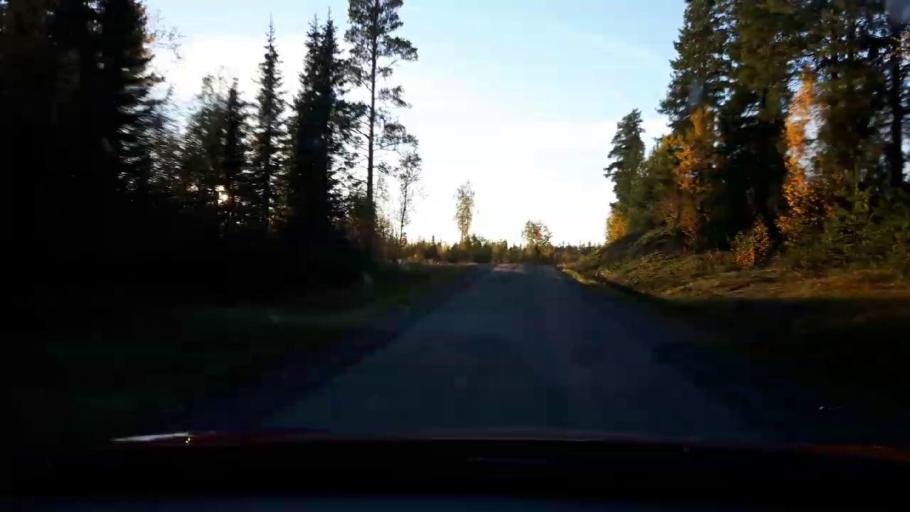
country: SE
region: Jaemtland
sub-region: Krokoms Kommun
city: Krokom
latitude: 63.4224
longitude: 14.4824
